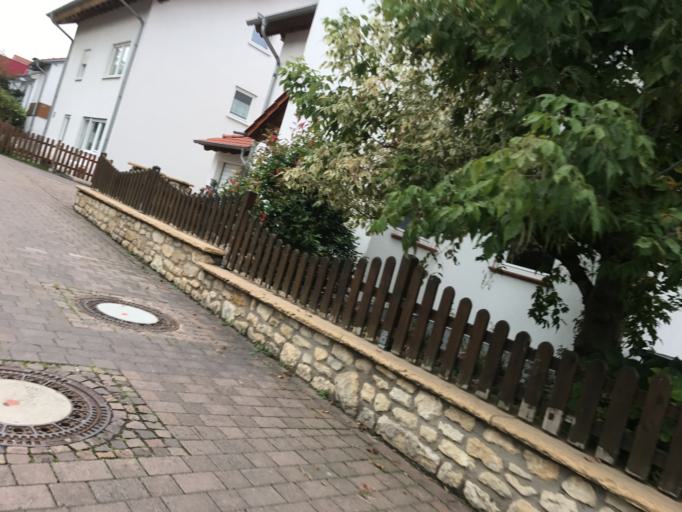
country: DE
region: Rheinland-Pfalz
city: Klein-Winternheim
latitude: 49.9366
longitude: 8.2136
